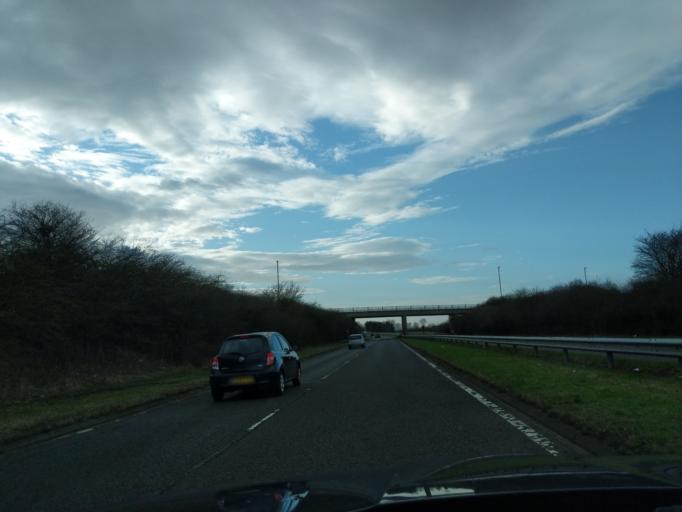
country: GB
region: England
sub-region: Northumberland
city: Seghill
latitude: 55.0492
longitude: -1.5849
